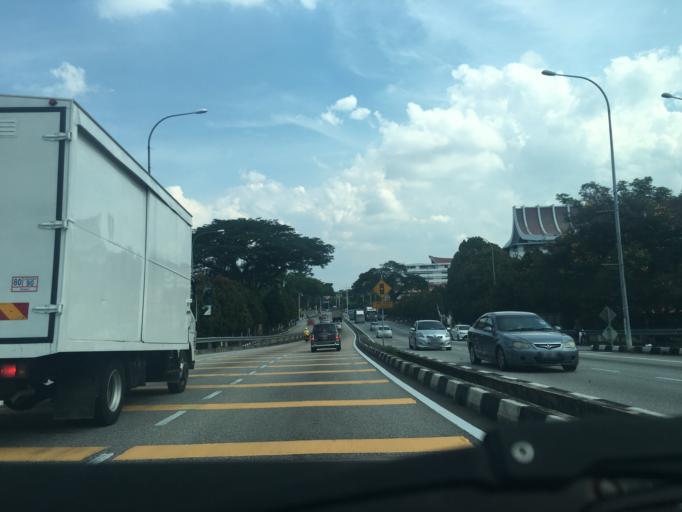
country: MY
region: Perak
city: Ipoh
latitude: 4.6076
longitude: 101.0782
